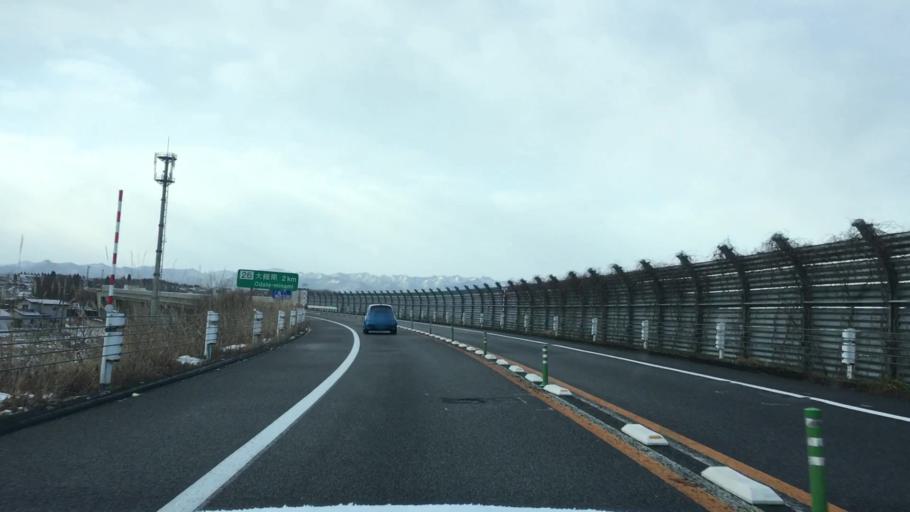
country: JP
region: Akita
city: Odate
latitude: 40.2878
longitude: 140.5422
